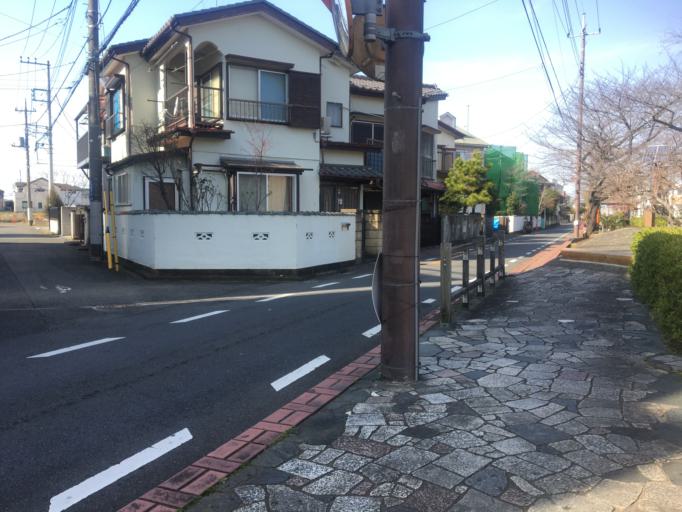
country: JP
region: Saitama
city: Shiki
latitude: 35.8338
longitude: 139.5882
